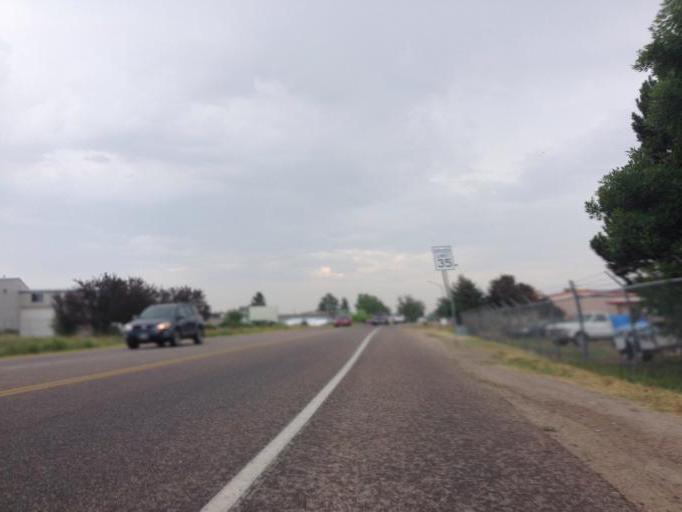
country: US
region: Colorado
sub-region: Larimer County
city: Fort Collins
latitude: 40.5861
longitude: -105.0491
